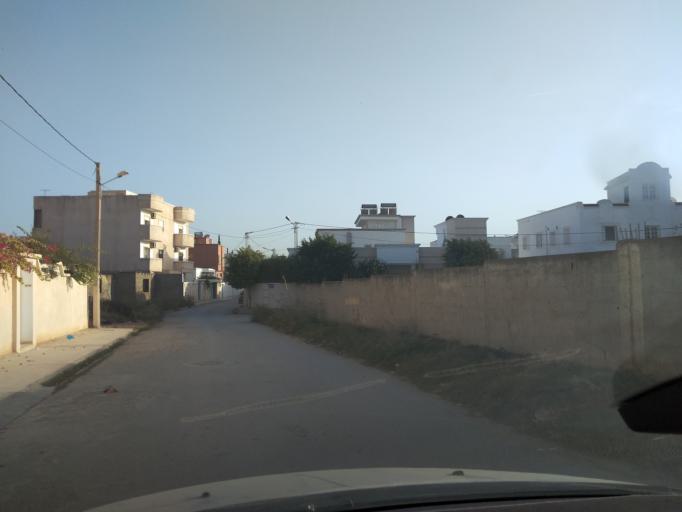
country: TN
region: Manouba
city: Manouba
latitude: 36.7950
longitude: 10.0850
